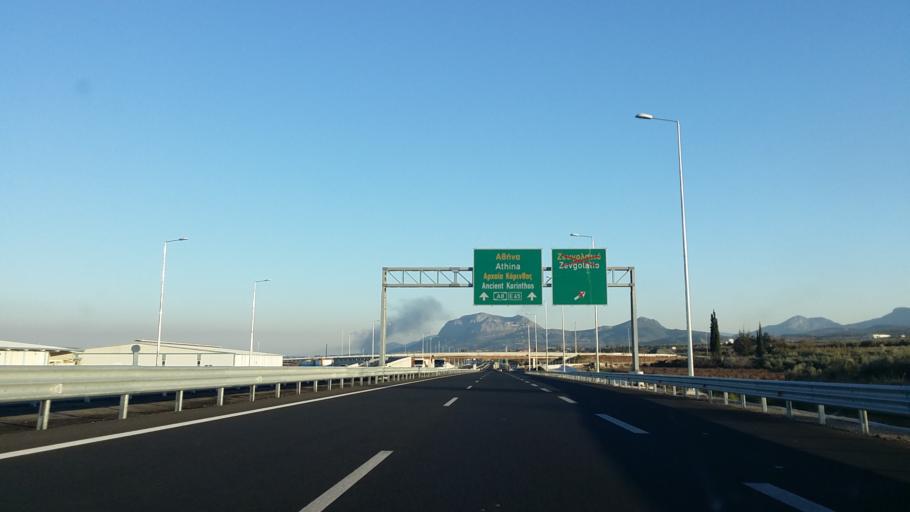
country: GR
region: Peloponnese
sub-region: Nomos Korinthias
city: Zevgolateio
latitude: 37.9306
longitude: 22.7855
